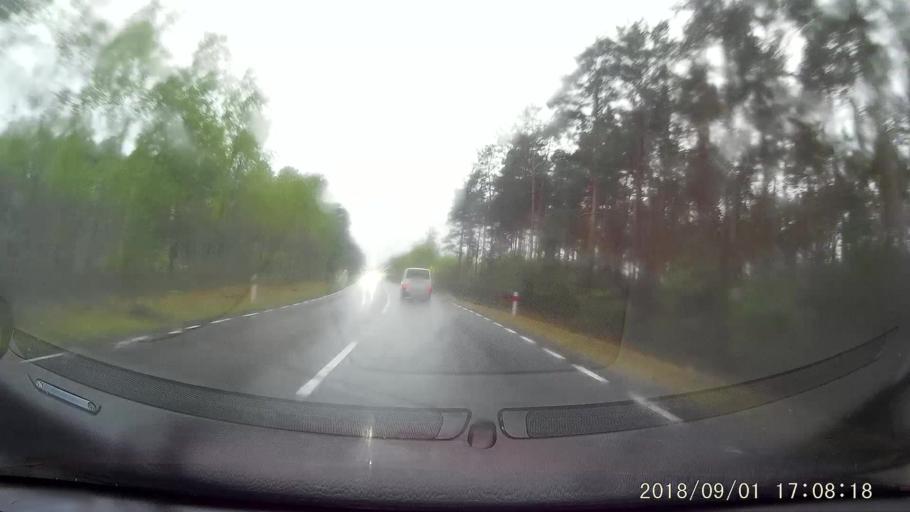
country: PL
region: Lubusz
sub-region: Powiat zielonogorski
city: Nowogrod Bobrzanski
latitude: 51.8303
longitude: 15.3096
